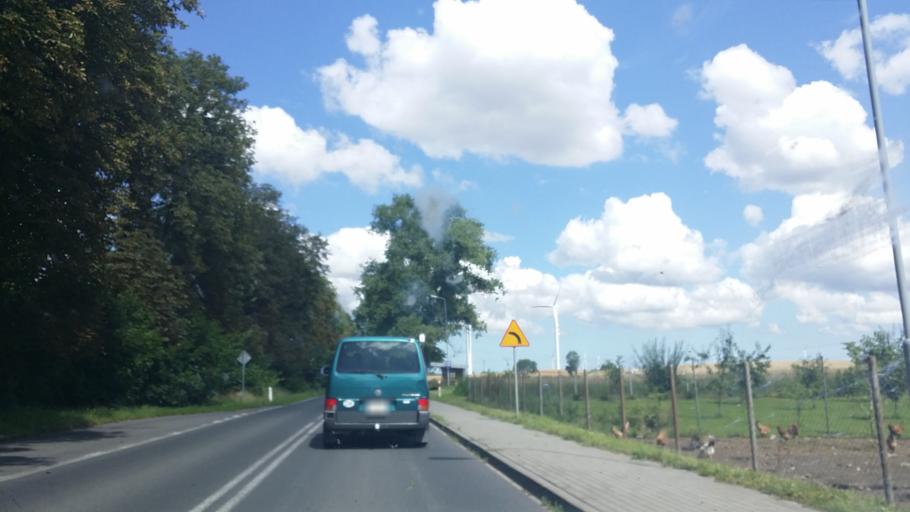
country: PL
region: West Pomeranian Voivodeship
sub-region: Powiat kolobrzeski
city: Goscino
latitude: 54.0014
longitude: 15.6744
